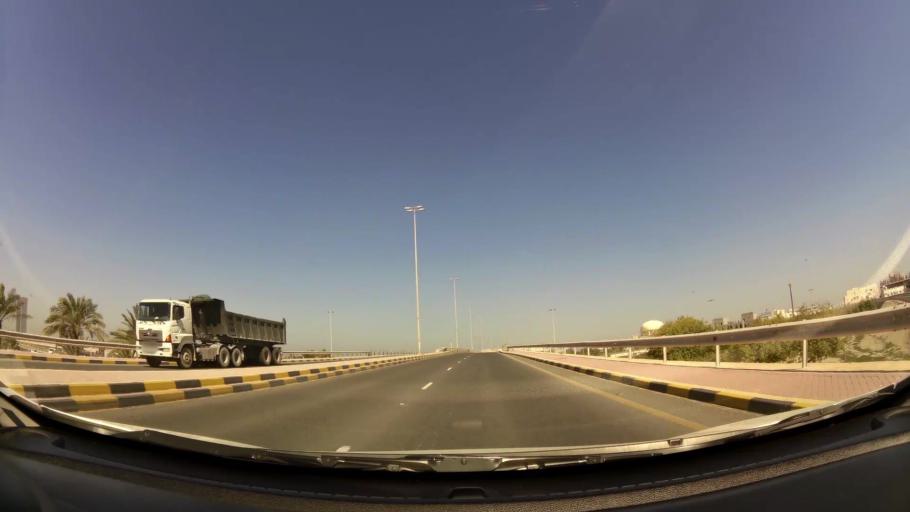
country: BH
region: Muharraq
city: Al Muharraq
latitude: 26.2493
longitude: 50.6062
